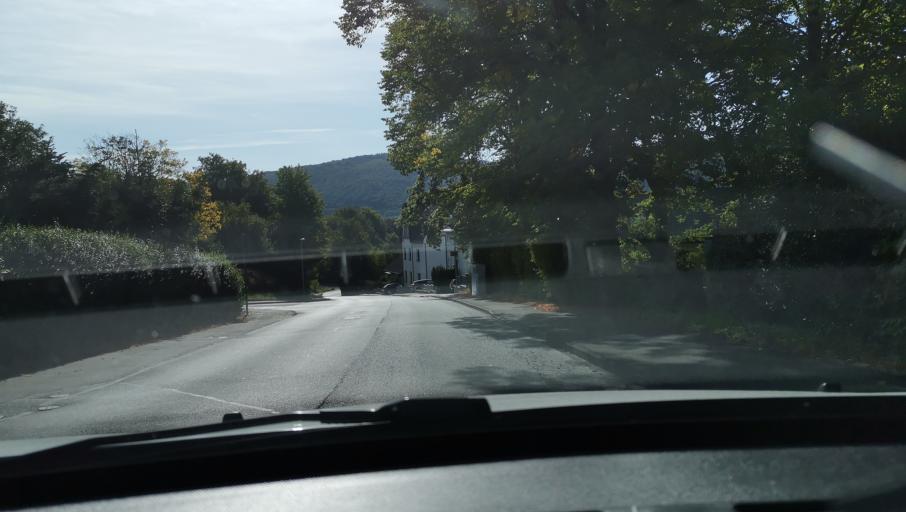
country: DE
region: North Rhine-Westphalia
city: Wetter (Ruhr)
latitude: 51.3421
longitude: 7.3816
